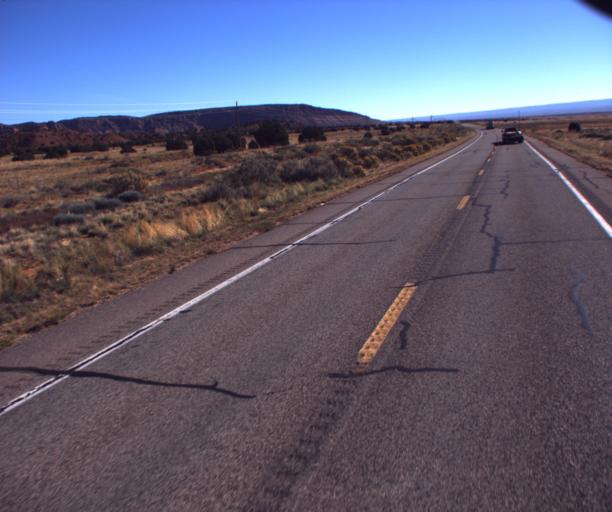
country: US
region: Arizona
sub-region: Mohave County
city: Colorado City
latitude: 36.8586
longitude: -112.8072
